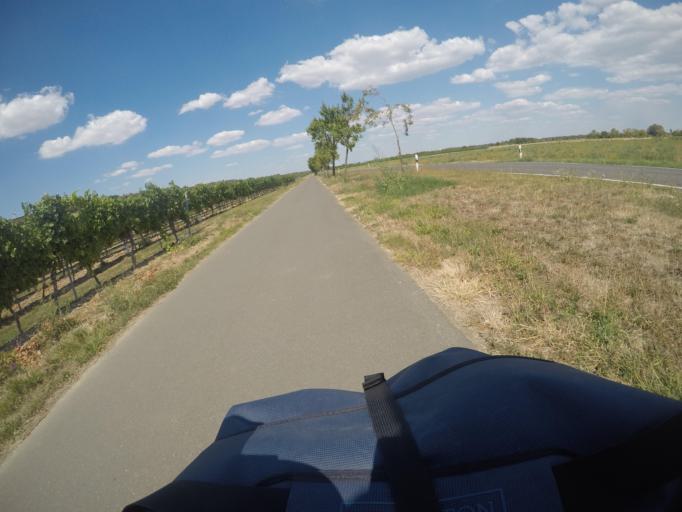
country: DE
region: Rheinland-Pfalz
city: Alsheim
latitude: 49.7756
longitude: 8.3415
